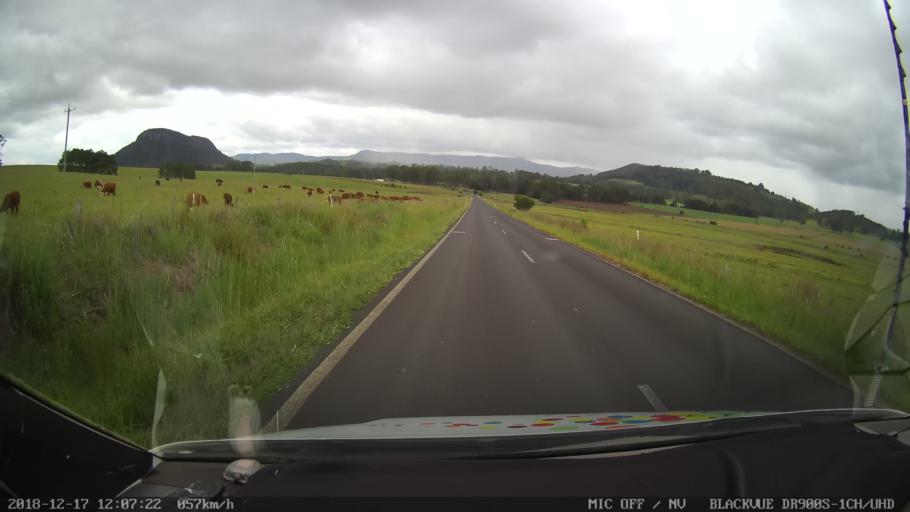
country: AU
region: New South Wales
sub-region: Kyogle
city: Kyogle
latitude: -28.4750
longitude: 152.5660
